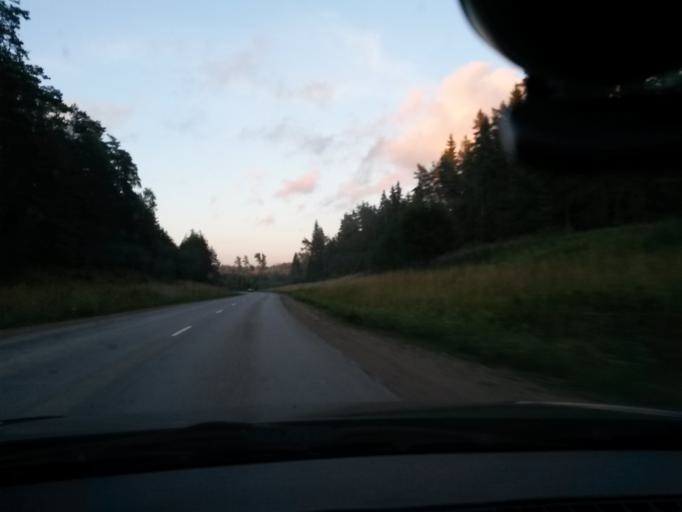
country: LV
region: Madonas Rajons
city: Madona
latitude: 56.8179
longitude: 26.1361
